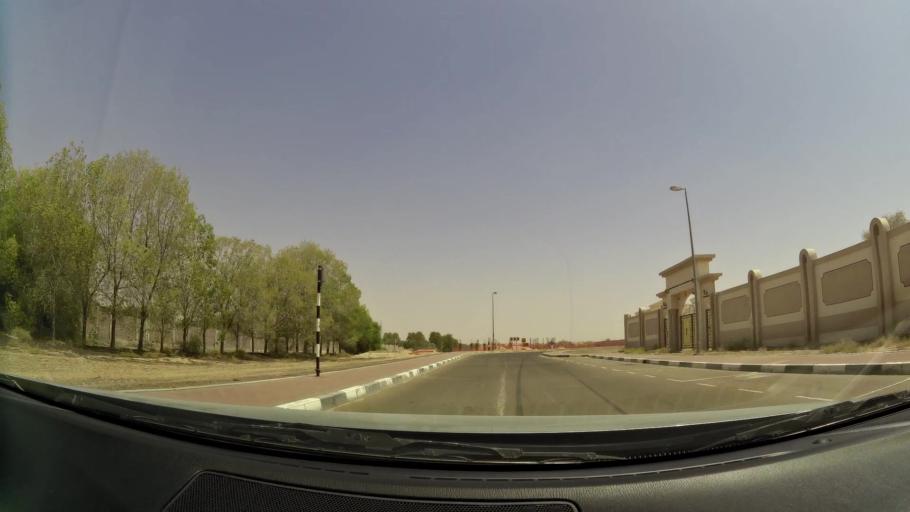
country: OM
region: Al Buraimi
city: Al Buraymi
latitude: 24.2867
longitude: 55.7550
